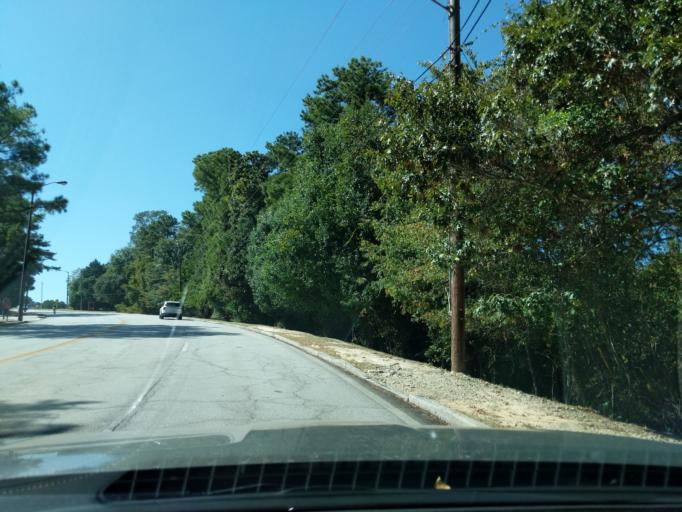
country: US
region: Georgia
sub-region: DeKalb County
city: Stone Mountain
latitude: 33.8135
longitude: -84.1399
